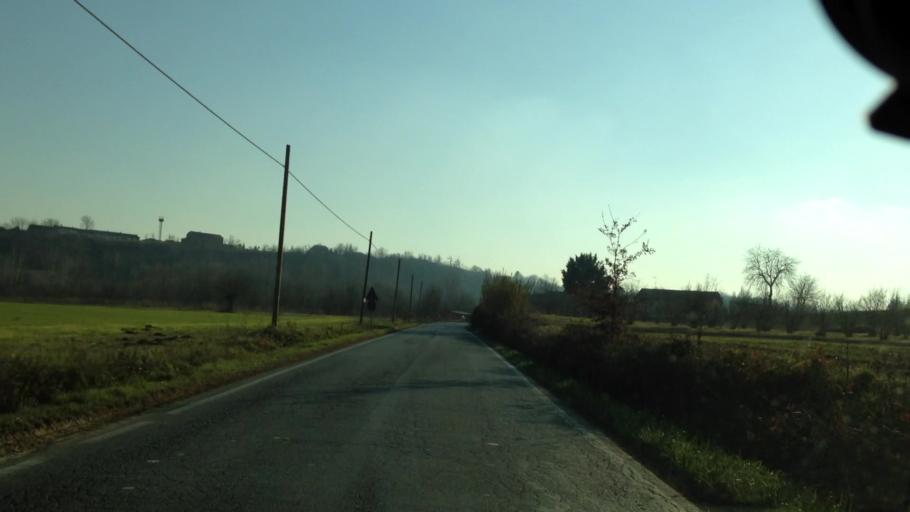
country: IT
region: Piedmont
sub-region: Provincia di Alessandria
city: Masio
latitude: 44.8666
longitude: 8.4164
